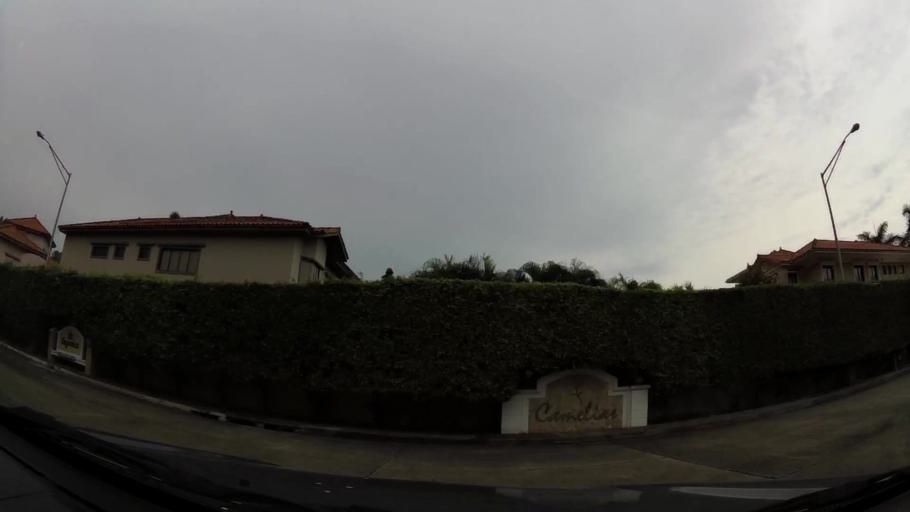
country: PA
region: Panama
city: San Miguelito
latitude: 9.0181
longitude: -79.4573
